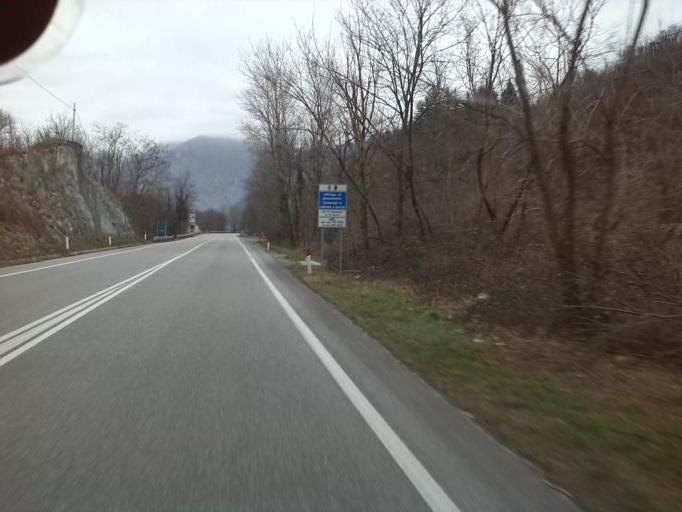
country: IT
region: Friuli Venezia Giulia
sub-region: Provincia di Udine
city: Bordano
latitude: 46.3032
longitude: 13.1209
